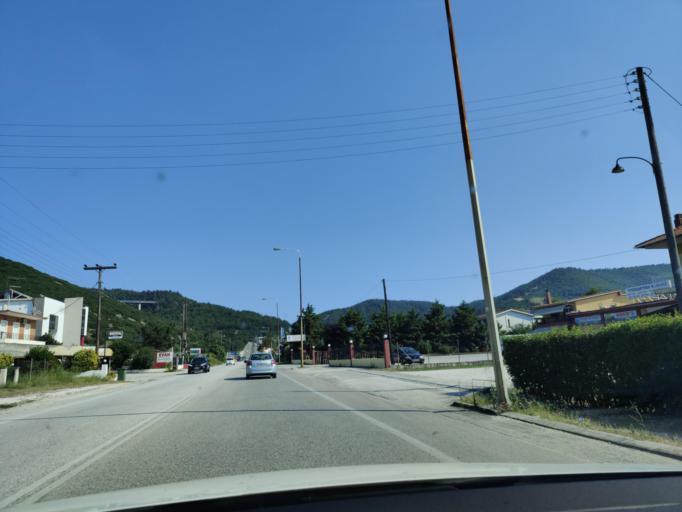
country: GR
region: East Macedonia and Thrace
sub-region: Nomos Kavalas
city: Amygdaleonas
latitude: 40.9572
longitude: 24.3640
